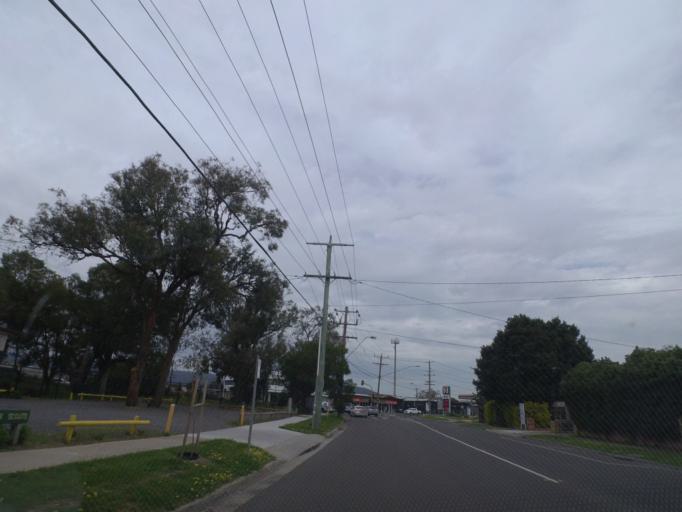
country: AU
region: Victoria
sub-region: Knox
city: Bayswater
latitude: -37.8440
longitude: 145.2694
